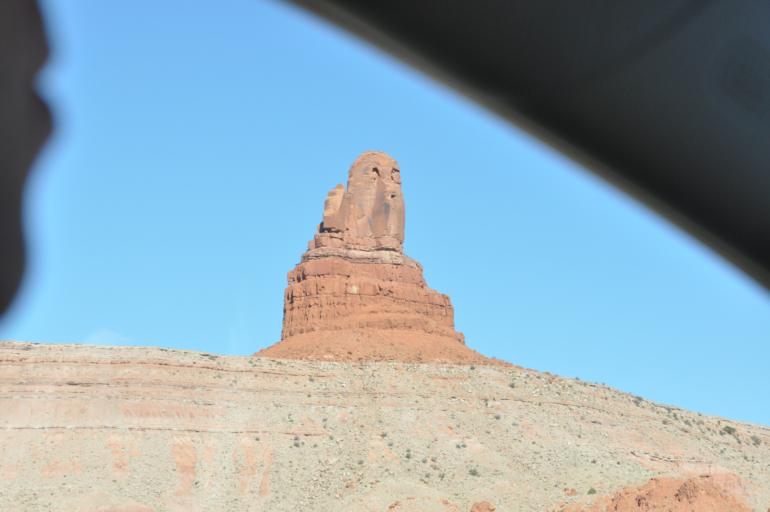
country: US
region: Arizona
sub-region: Navajo County
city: Kayenta
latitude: 36.8398
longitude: -110.2627
